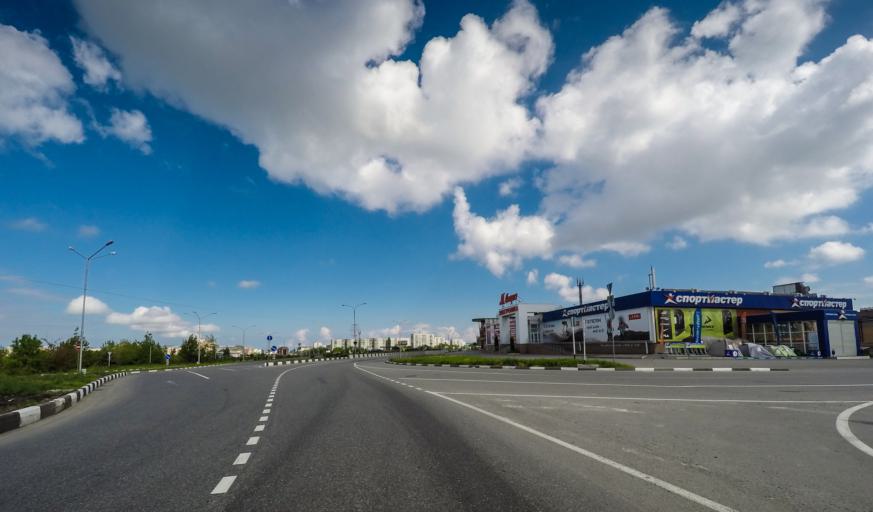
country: RU
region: North Ossetia
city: Vladikavkaz
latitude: 43.0315
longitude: 44.6430
